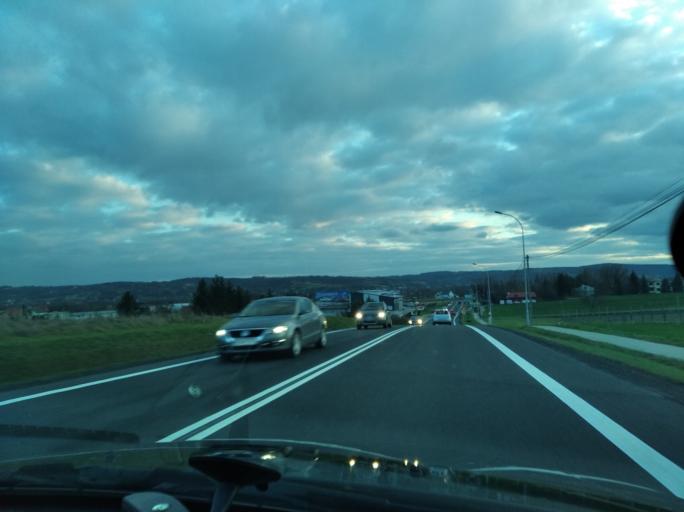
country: PL
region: Subcarpathian Voivodeship
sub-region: Powiat rzeszowski
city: Lutoryz
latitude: 49.9671
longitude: 21.9217
